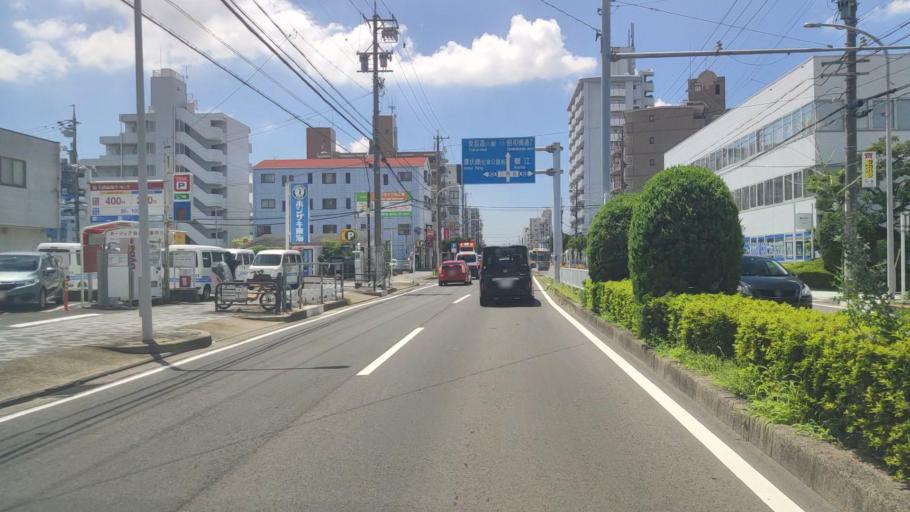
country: JP
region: Aichi
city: Kanie
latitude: 35.1422
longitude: 136.8534
